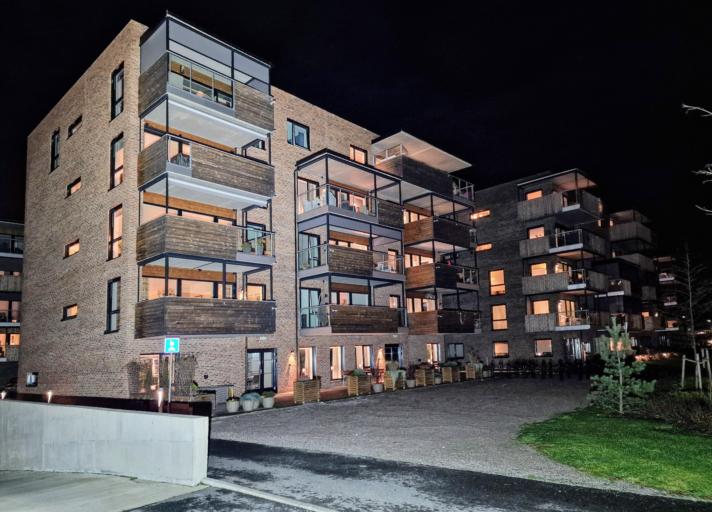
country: NO
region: Akershus
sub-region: Skedsmo
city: Lillestrom
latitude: 60.0031
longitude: 11.0329
